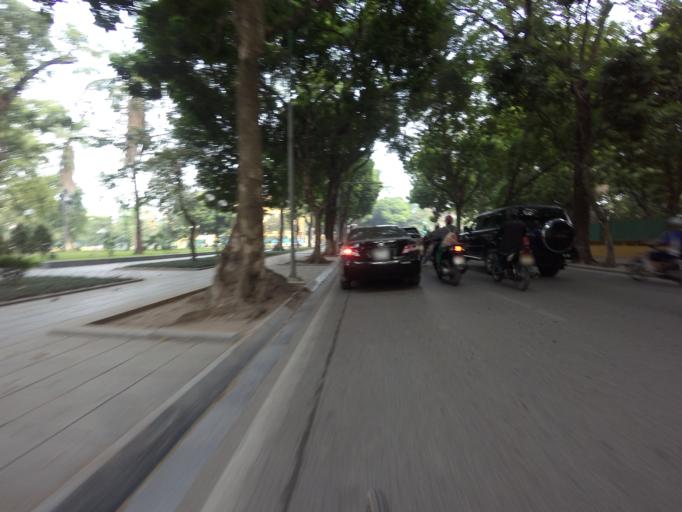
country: VN
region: Ha Noi
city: Hanoi
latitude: 21.0419
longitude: 105.8356
